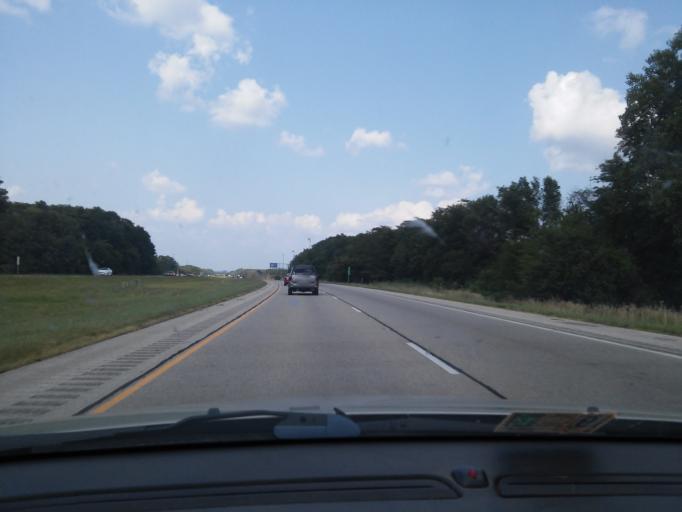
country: US
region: Illinois
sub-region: McLean County
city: Twin Grove
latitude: 40.3562
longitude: -89.1102
